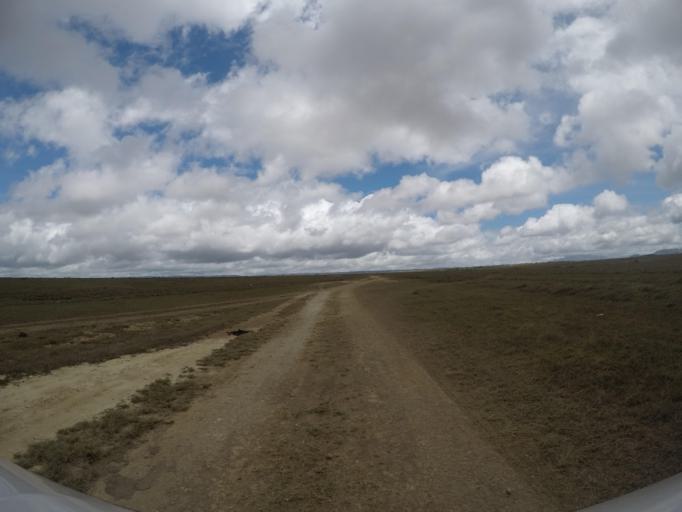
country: TL
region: Lautem
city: Lospalos
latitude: -8.4503
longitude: 126.9865
